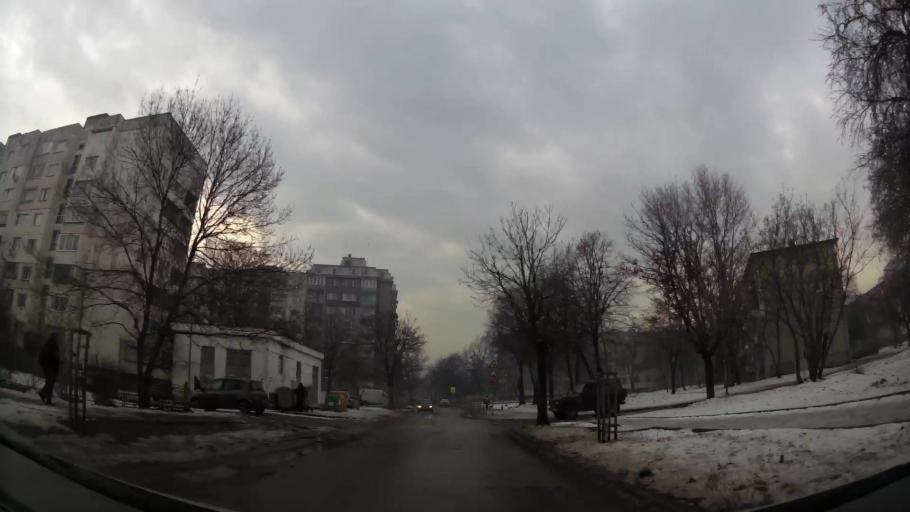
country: BG
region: Sofia-Capital
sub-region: Stolichna Obshtina
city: Sofia
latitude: 42.6946
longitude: 23.2798
